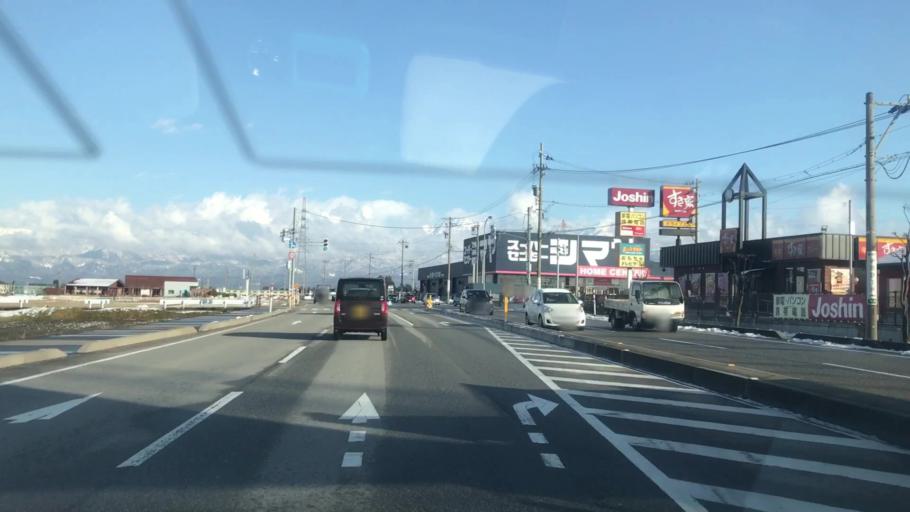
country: JP
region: Toyama
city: Kamiichi
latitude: 36.6863
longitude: 137.2930
